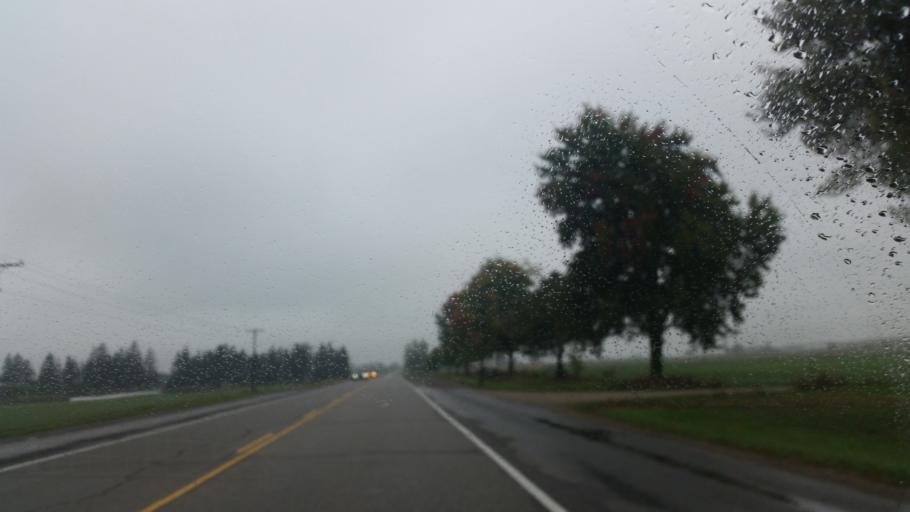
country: CA
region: Ontario
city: Waterloo
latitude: 43.5957
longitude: -80.5148
